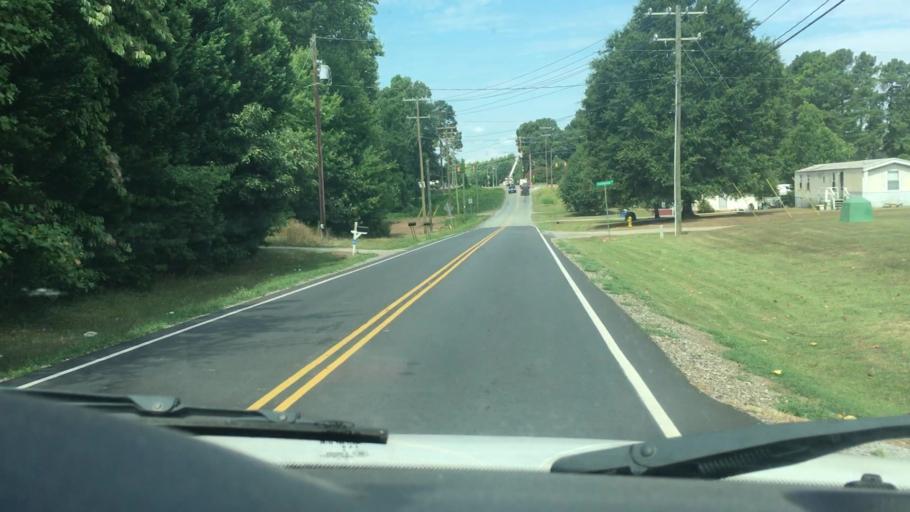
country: US
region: North Carolina
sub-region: Gaston County
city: Davidson
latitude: 35.5429
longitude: -80.8443
